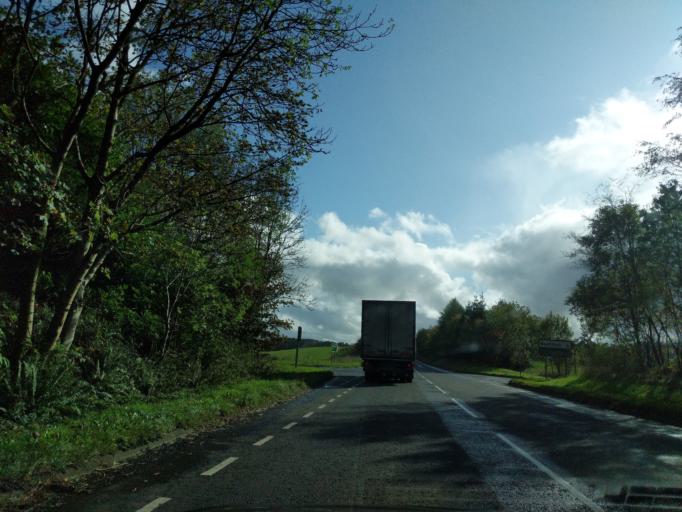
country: GB
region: Scotland
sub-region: Dumfries and Galloway
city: Moffat
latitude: 55.3013
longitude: -3.4458
